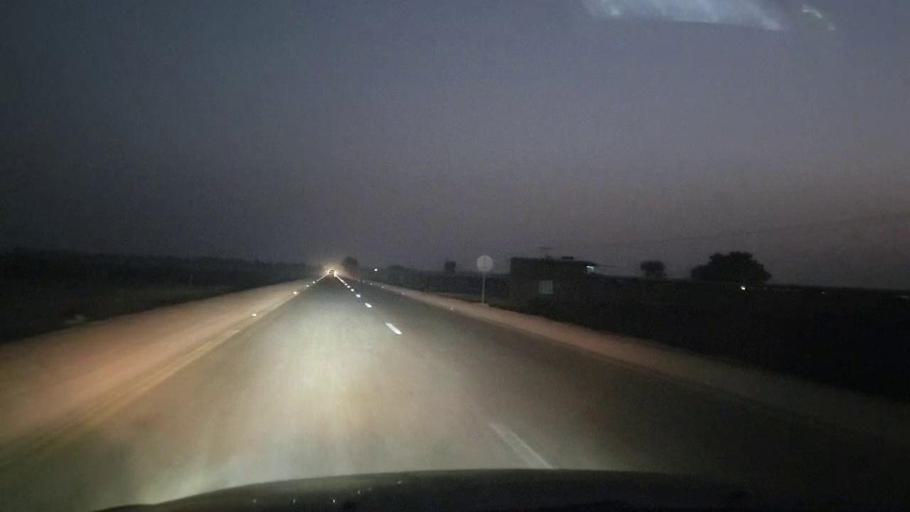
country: PK
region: Sindh
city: Chambar
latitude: 25.3313
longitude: 68.7981
